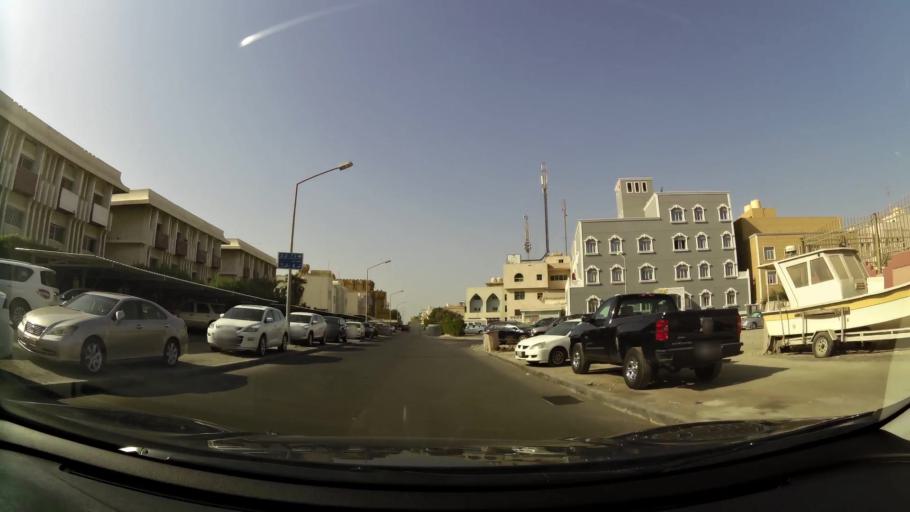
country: KW
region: Muhafazat Hawalli
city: Salwa
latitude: 29.2923
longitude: 48.0721
